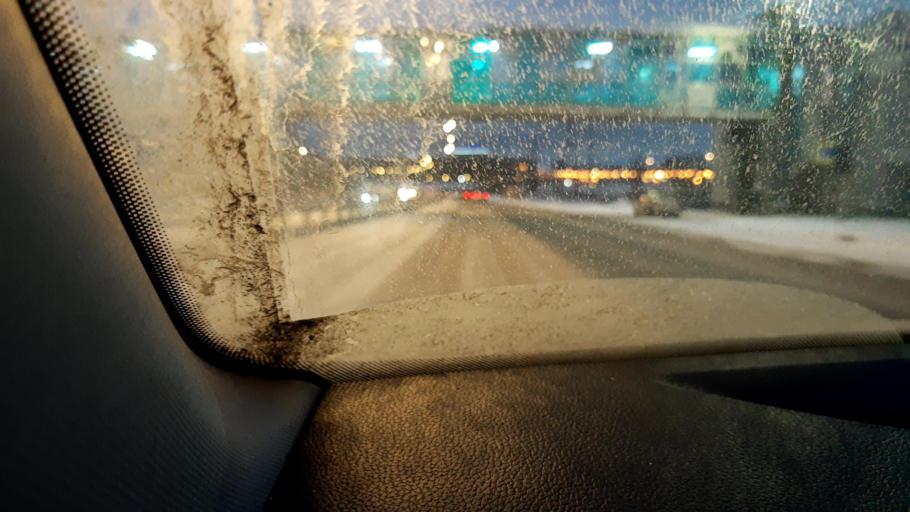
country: RU
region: Moscow
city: Tyoply Stan
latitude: 55.5978
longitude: 37.4847
